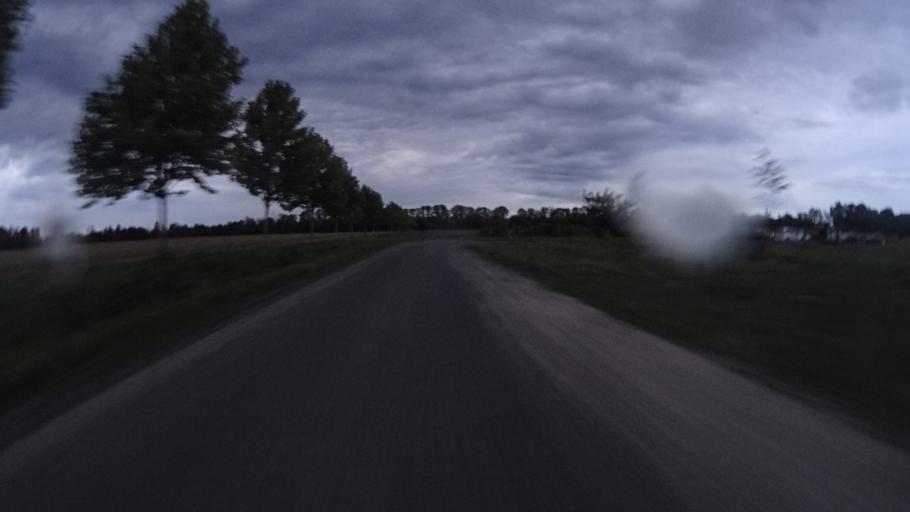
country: PL
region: Masovian Voivodeship
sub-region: Powiat warszawski zachodni
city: Ozarow Mazowiecki
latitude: 52.2330
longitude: 20.7964
